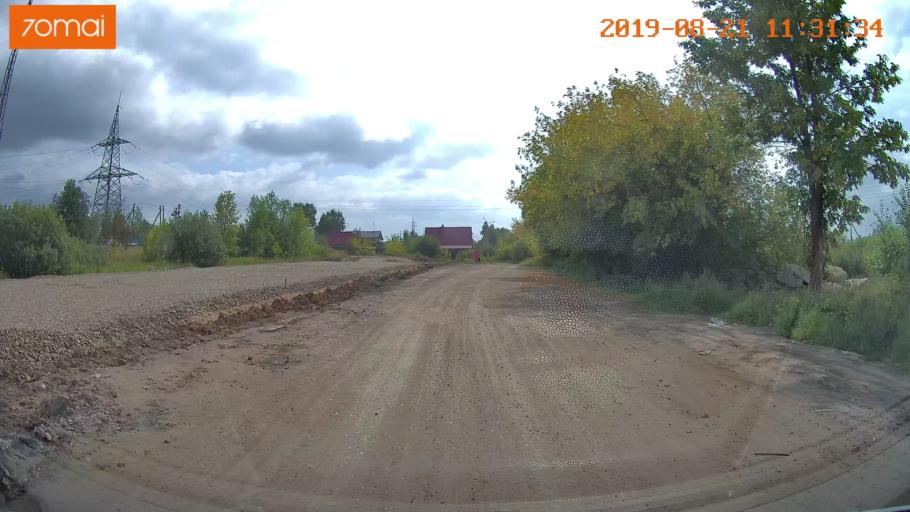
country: RU
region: Ivanovo
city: Novo-Talitsy
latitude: 56.9876
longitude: 40.9080
